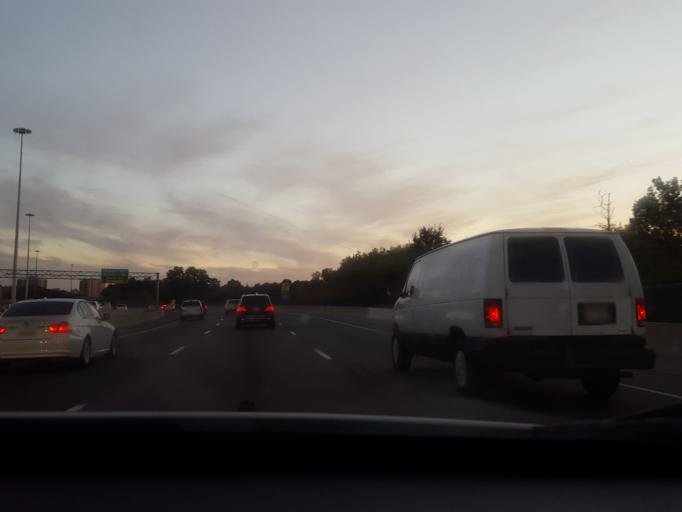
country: CA
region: Ontario
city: North York
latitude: 43.7501
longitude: -79.4142
